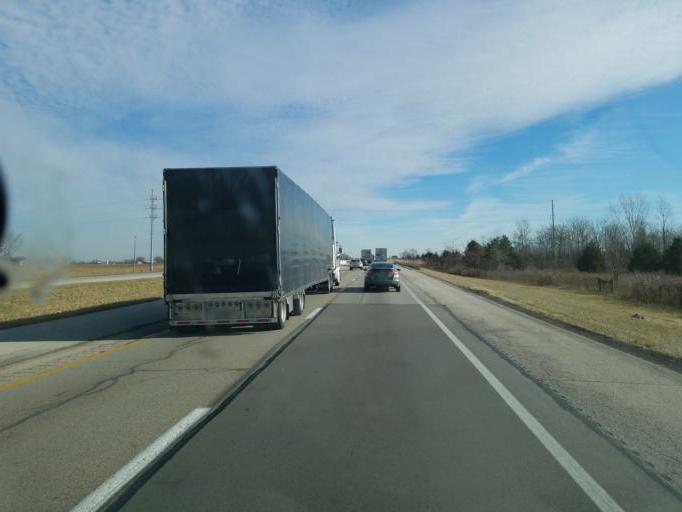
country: US
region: Ohio
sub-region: Preble County
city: Lewisburg
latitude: 39.8355
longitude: -84.6164
